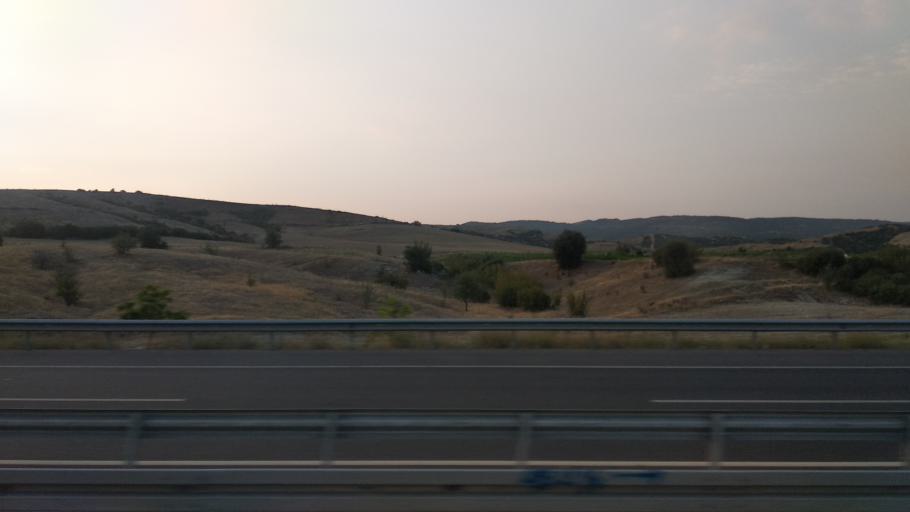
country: TR
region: Manisa
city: Selendi
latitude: 38.6243
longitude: 28.9286
